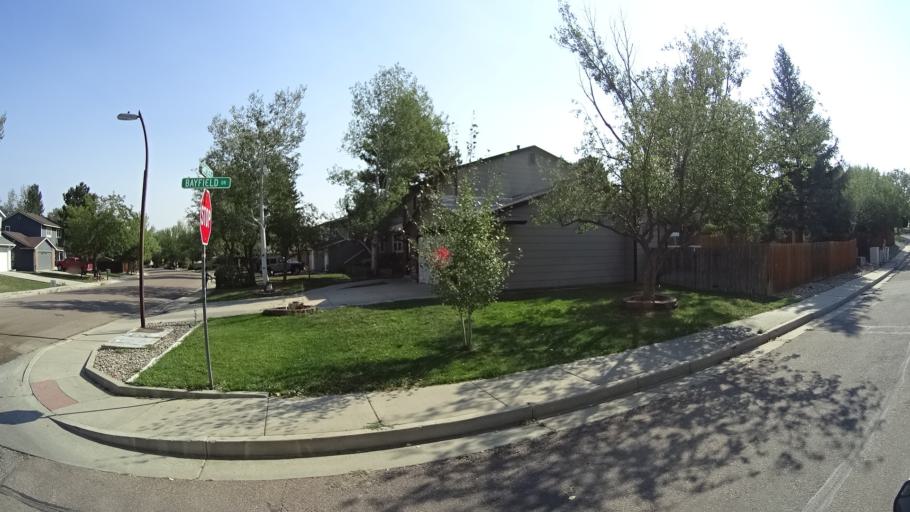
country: US
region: Colorado
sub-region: El Paso County
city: Stratmoor
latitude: 38.7826
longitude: -104.8149
